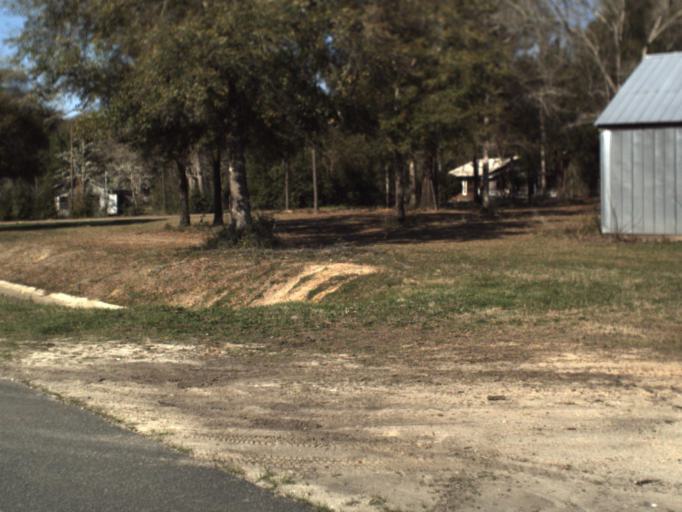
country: US
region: Florida
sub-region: Gulf County
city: Wewahitchka
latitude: 30.2654
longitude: -85.2418
